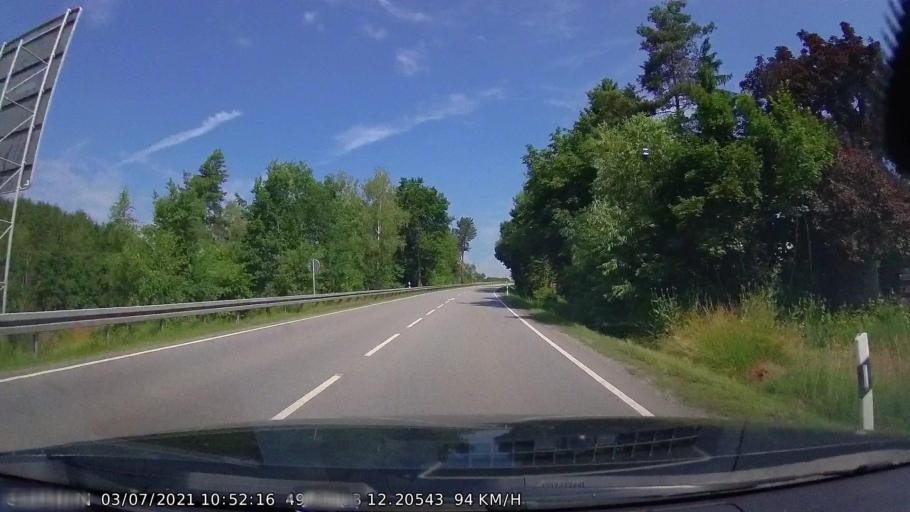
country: DE
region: Bavaria
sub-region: Upper Palatinate
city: Bechtsrieth
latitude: 49.6474
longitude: 12.2053
